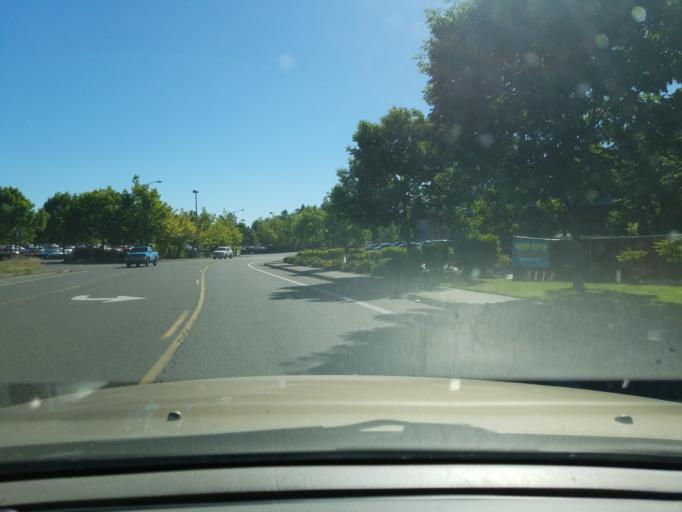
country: US
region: Oregon
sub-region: Yamhill County
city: McMinnville
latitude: 45.1929
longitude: -123.2108
